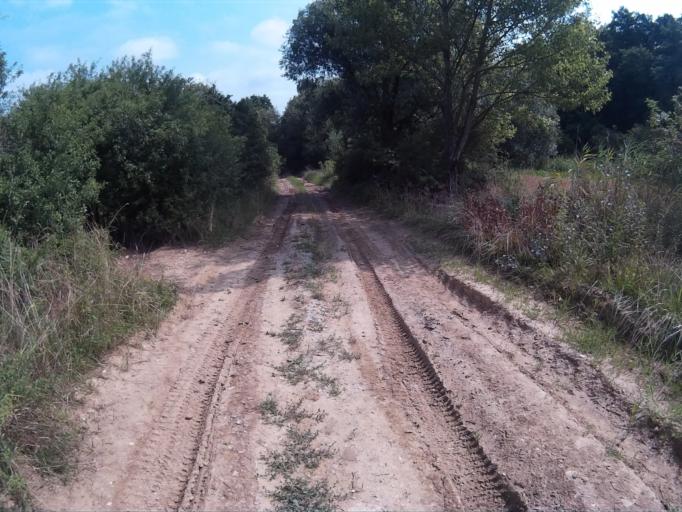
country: HU
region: Veszprem
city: Papa
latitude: 47.2923
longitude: 17.5879
